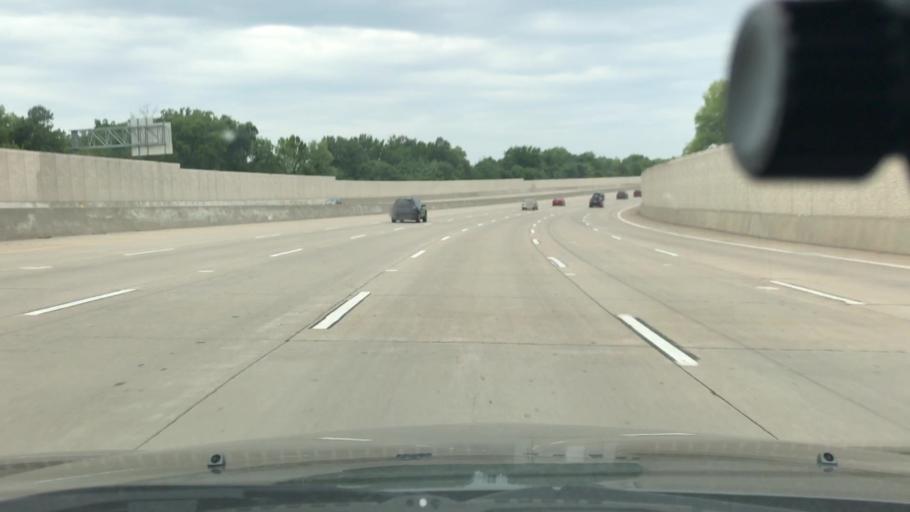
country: US
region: Missouri
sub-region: Saint Louis County
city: Maryland Heights
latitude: 38.6967
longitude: -90.4683
